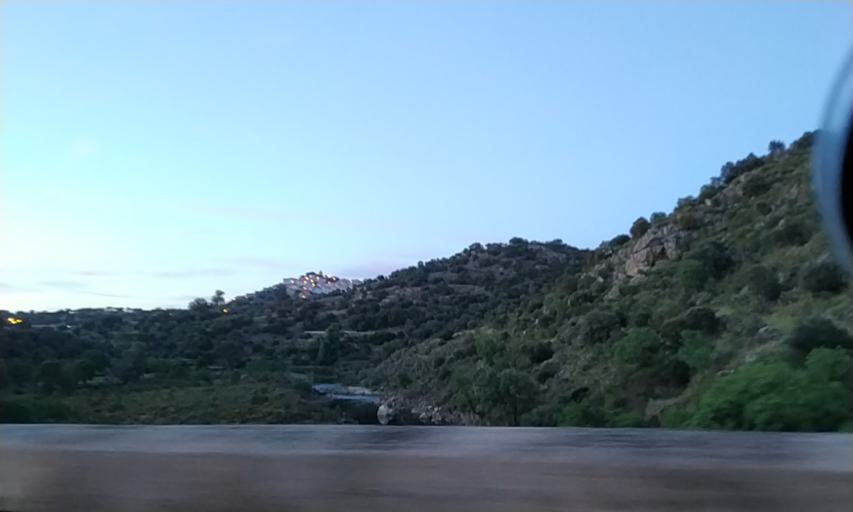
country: ES
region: Extremadura
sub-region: Provincia de Caceres
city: Piedras Albas
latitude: 39.8172
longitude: -6.9816
